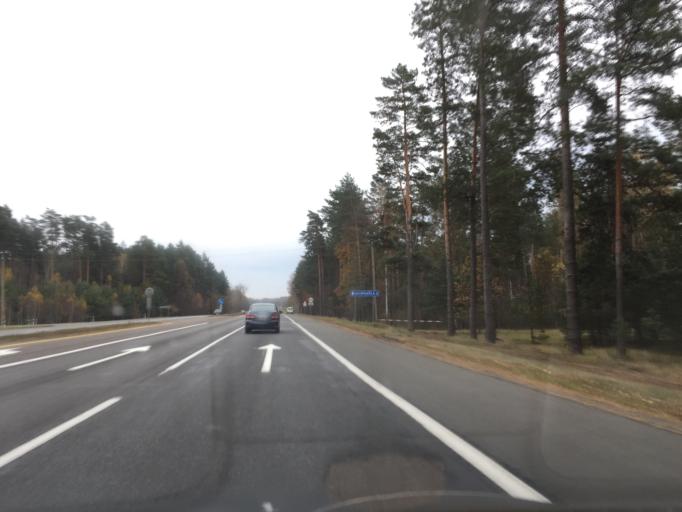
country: BY
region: Gomel
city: Horad Rechytsa
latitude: 52.3593
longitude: 30.6627
